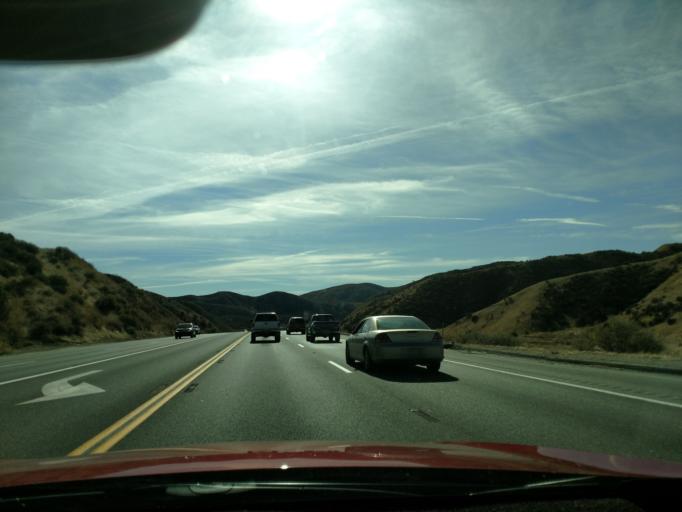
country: US
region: California
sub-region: Riverside County
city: Beaumont
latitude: 33.8827
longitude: -116.9909
